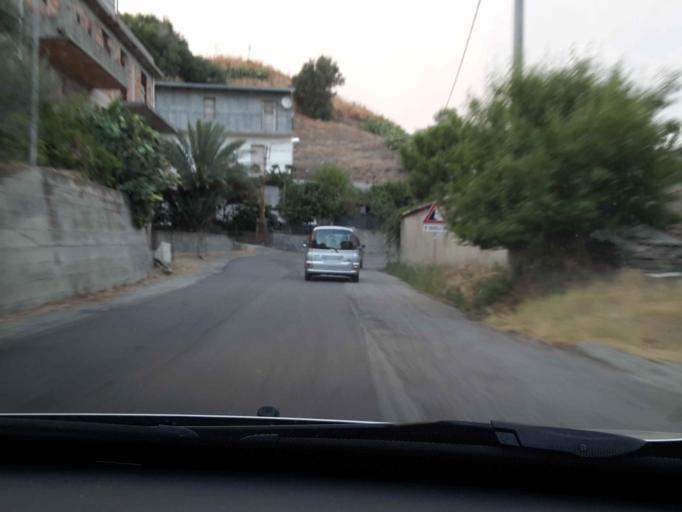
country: IT
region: Calabria
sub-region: Provincia di Reggio Calabria
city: San Lorenzo
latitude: 37.9757
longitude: 15.8048
